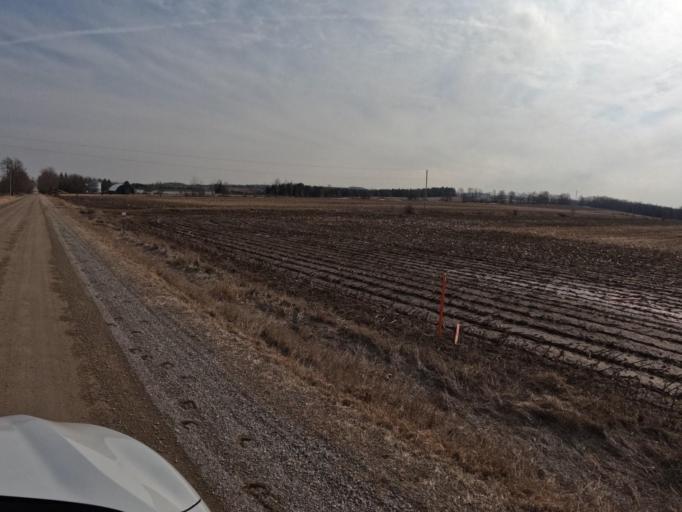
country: CA
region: Ontario
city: Orangeville
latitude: 43.9027
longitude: -80.2684
